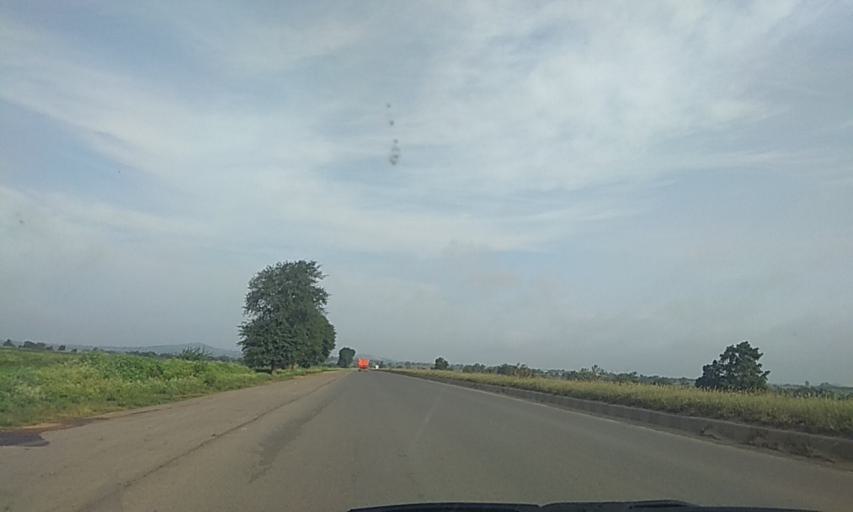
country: IN
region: Karnataka
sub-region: Haveri
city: Byadgi
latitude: 14.7261
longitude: 75.4723
